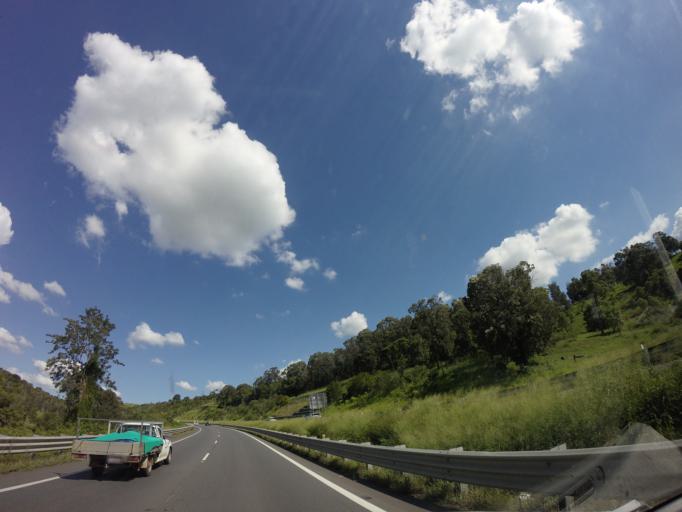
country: AU
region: Queensland
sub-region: Ipswich
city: Thagoona
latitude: -27.5632
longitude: 152.5554
